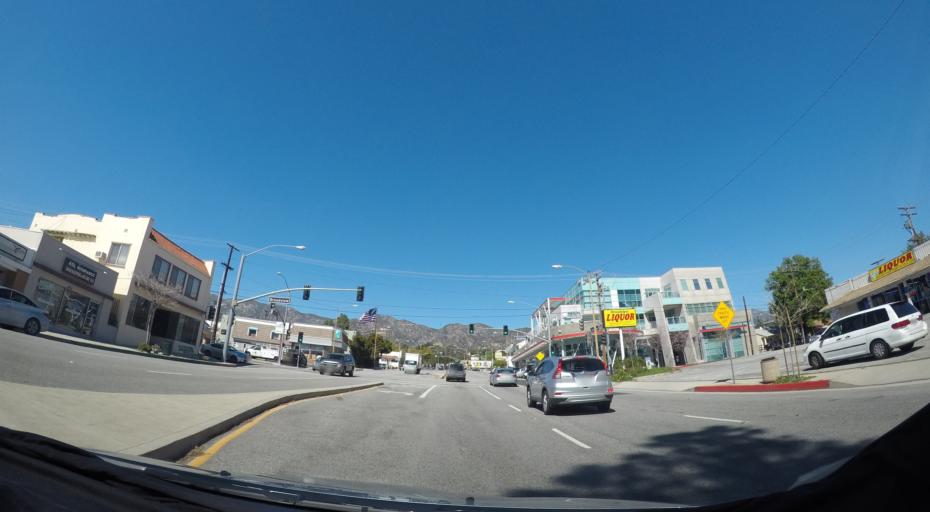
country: US
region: California
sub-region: Los Angeles County
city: La Crescenta-Montrose
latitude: 34.2040
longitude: -118.2271
